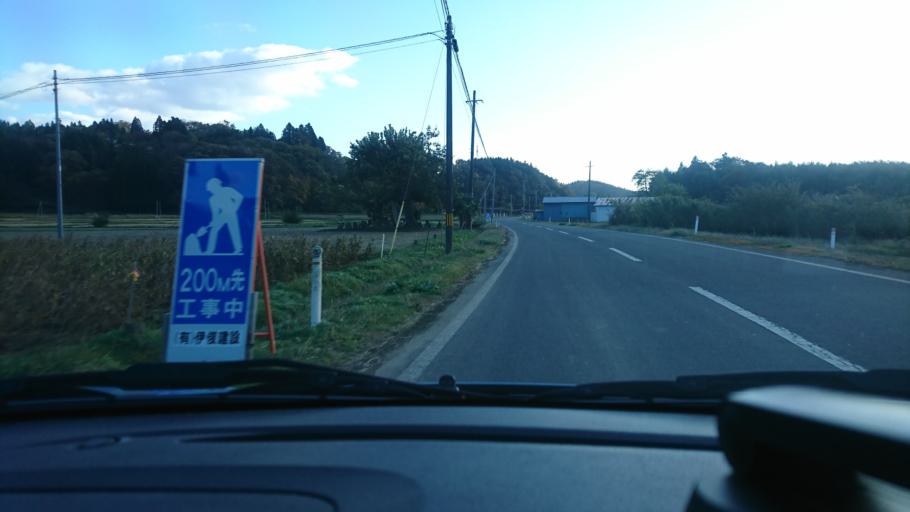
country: JP
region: Iwate
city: Ichinoseki
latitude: 38.8014
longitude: 141.2491
